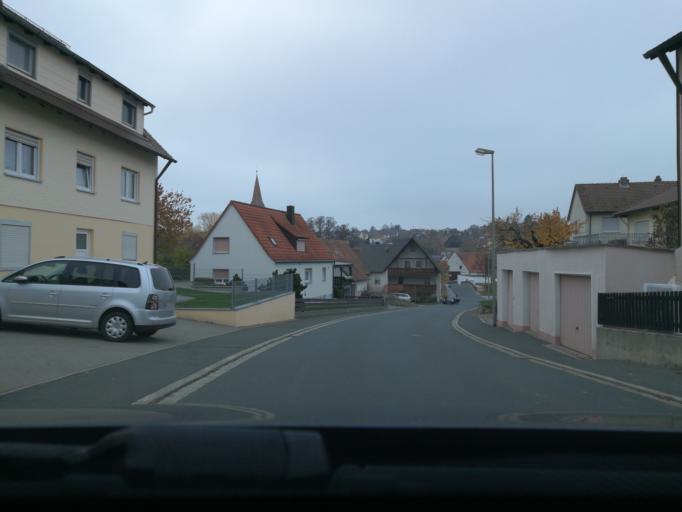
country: DE
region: Bavaria
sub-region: Regierungsbezirk Mittelfranken
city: Puschendorf
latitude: 49.5728
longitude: 10.8257
